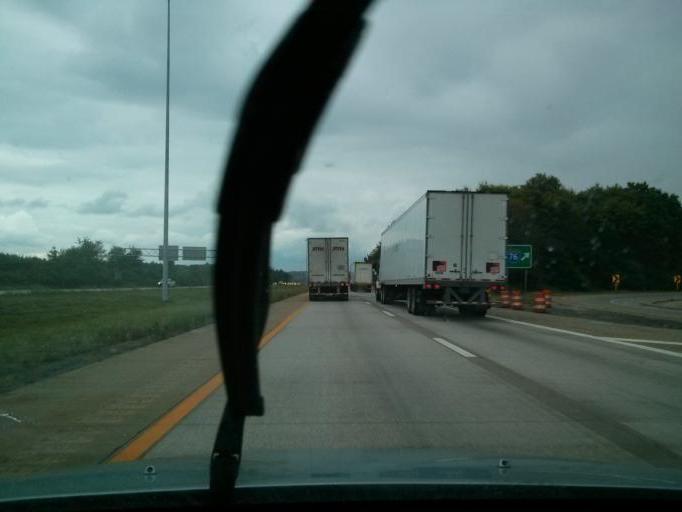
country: US
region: Ohio
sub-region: Trumbull County
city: Lordstown
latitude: 41.1104
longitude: -80.8305
